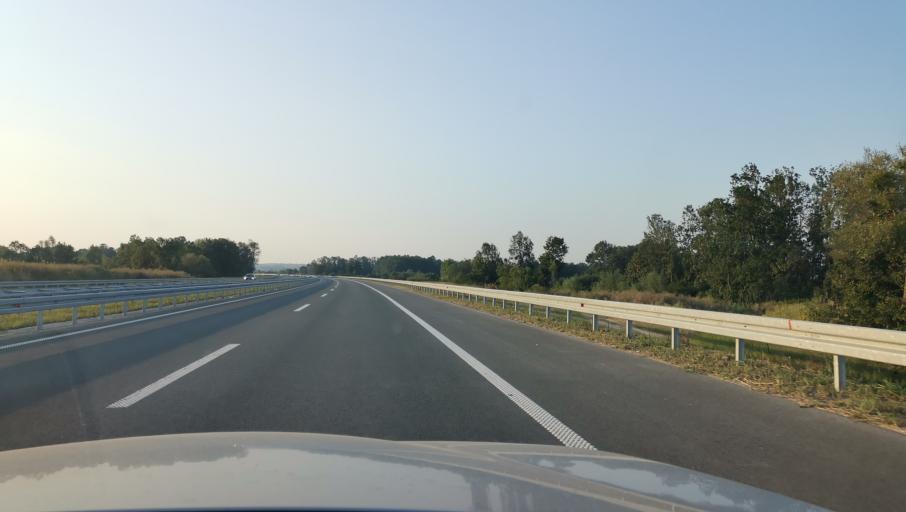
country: RS
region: Central Serbia
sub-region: Kolubarski Okrug
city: Ljig
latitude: 44.2647
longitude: 20.2706
